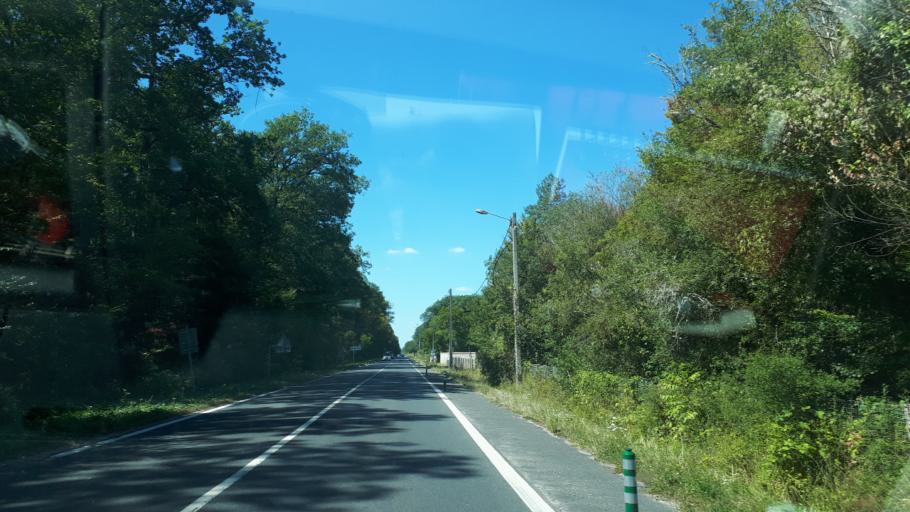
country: FR
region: Centre
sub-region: Departement du Loir-et-Cher
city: Mont-pres-Chambord
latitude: 47.5625
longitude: 1.4372
